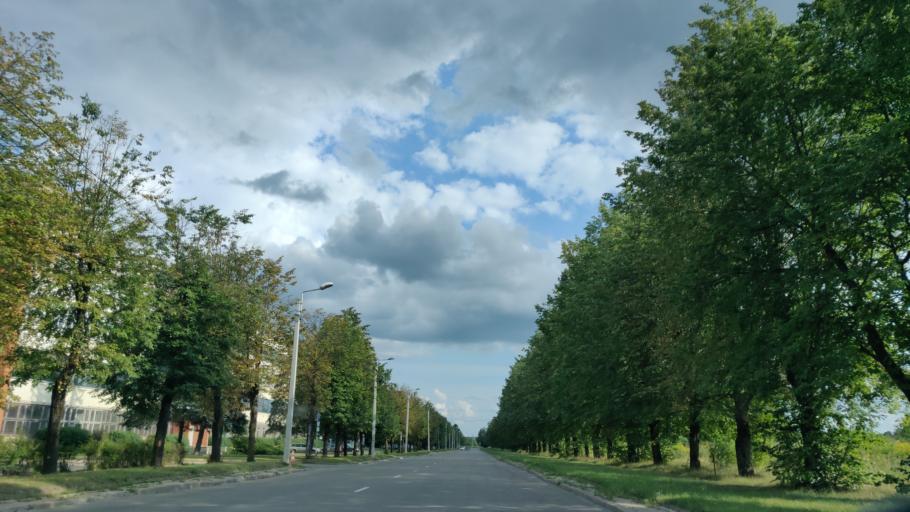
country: LT
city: Baltoji Voke
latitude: 54.6241
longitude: 25.1411
